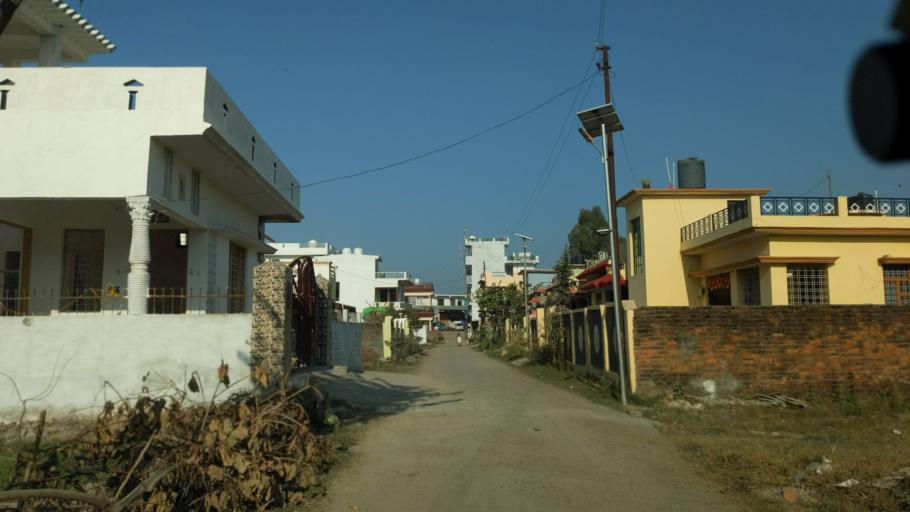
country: IN
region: Uttarakhand
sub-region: Naini Tal
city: Haldwani
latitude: 29.2072
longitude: 79.4959
